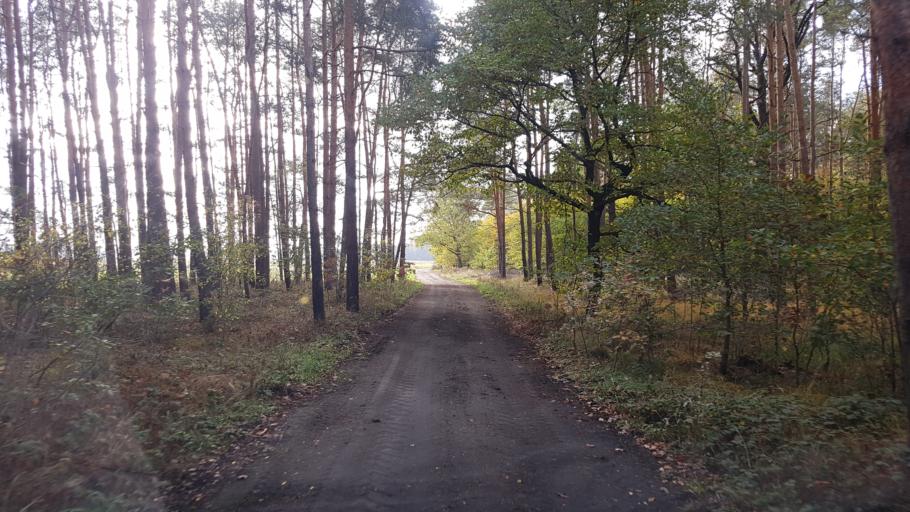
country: DE
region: Brandenburg
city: Schonborn
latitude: 51.5777
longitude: 13.5079
